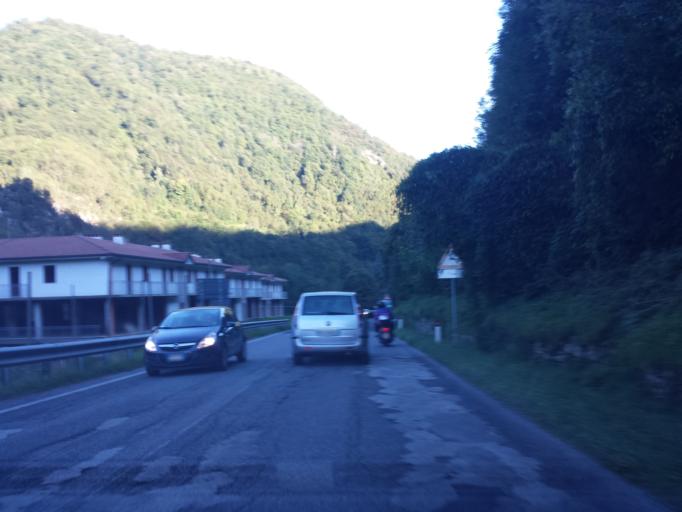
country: IT
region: Veneto
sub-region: Provincia di Vicenza
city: San Quirico
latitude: 45.6857
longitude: 11.2676
